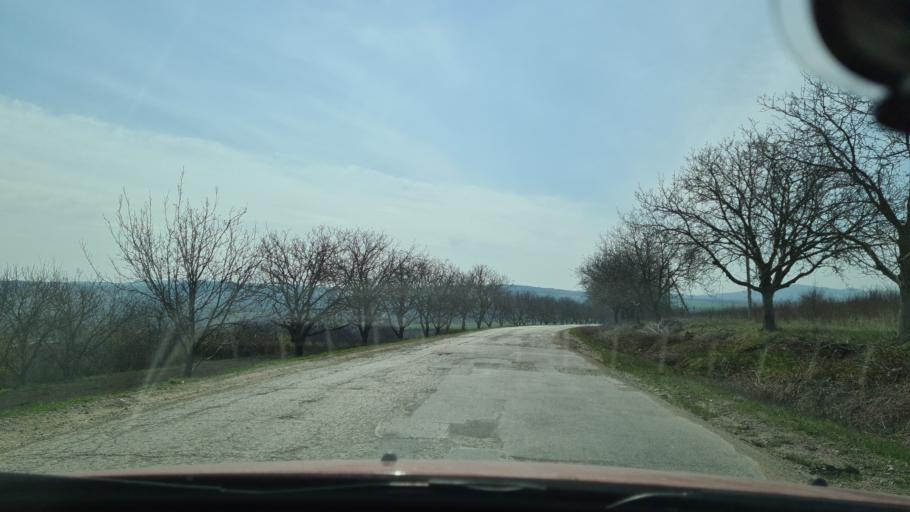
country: MD
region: Ungheni
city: Ungheni
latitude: 47.2881
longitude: 27.9216
